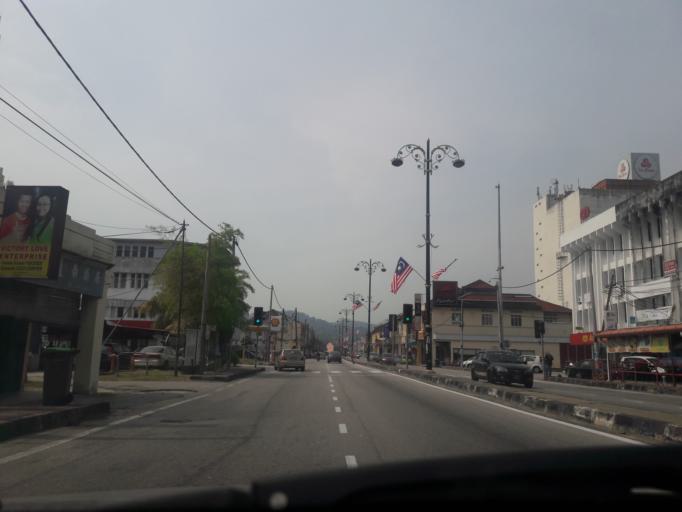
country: MY
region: Kedah
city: Kulim
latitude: 5.3726
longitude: 100.5551
